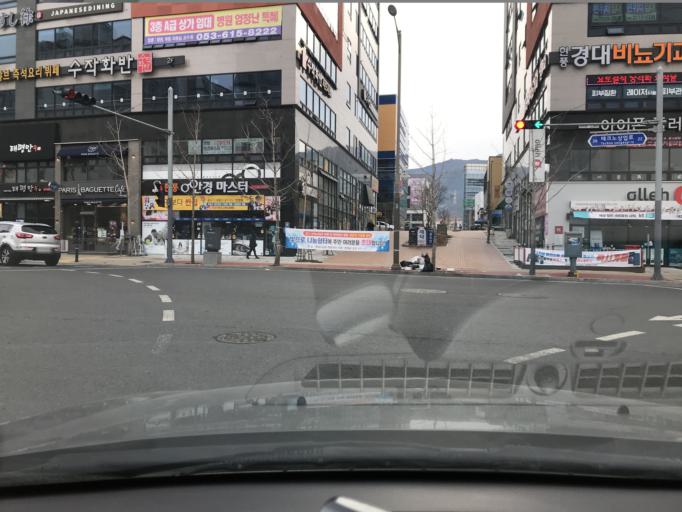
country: KR
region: Daegu
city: Hwawon
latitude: 35.6912
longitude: 128.4529
